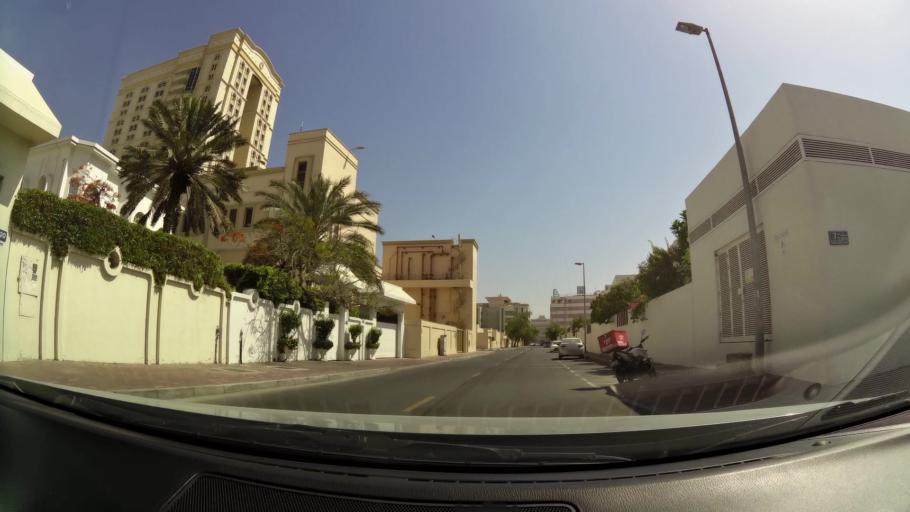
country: AE
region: Ash Shariqah
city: Sharjah
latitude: 25.2357
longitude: 55.2728
